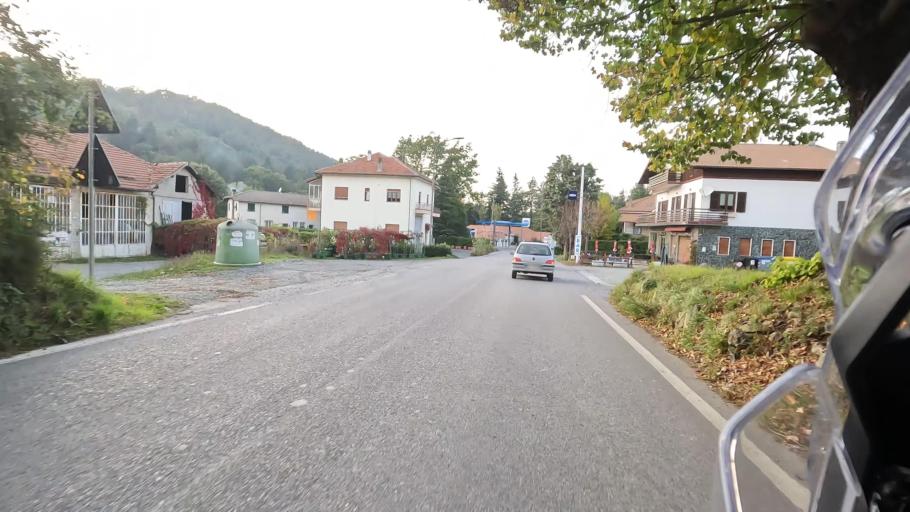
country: IT
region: Liguria
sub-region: Provincia di Savona
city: Sassello
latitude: 44.4761
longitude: 8.4863
